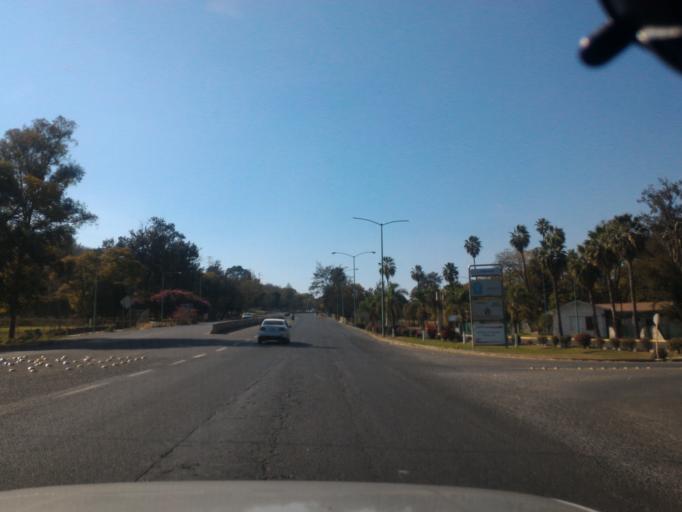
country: MX
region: Jalisco
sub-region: Poncitlan
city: Cuitzeo (La Estancia)
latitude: 20.3477
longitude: -102.7869
